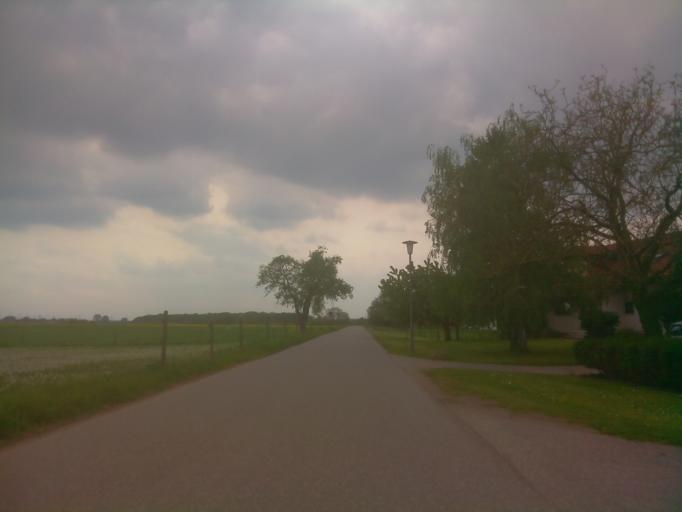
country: DE
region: Baden-Wuerttemberg
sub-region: Karlsruhe Region
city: Eppelheim
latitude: 49.3899
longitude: 8.6208
